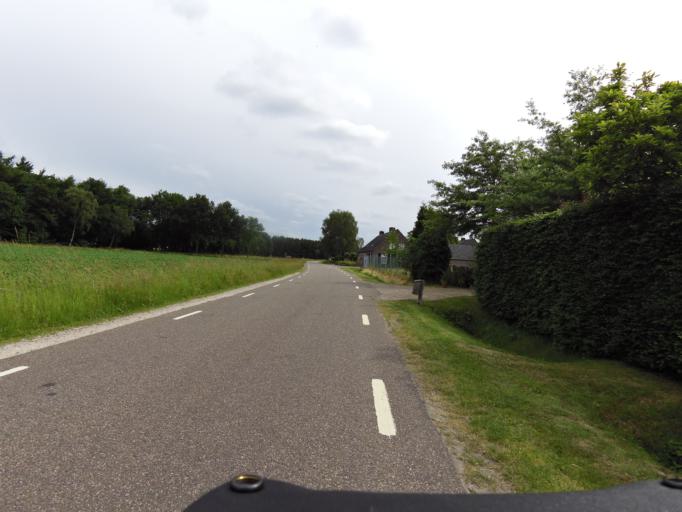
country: BE
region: Flanders
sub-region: Provincie Antwerpen
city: Arendonk
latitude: 51.3970
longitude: 5.1205
